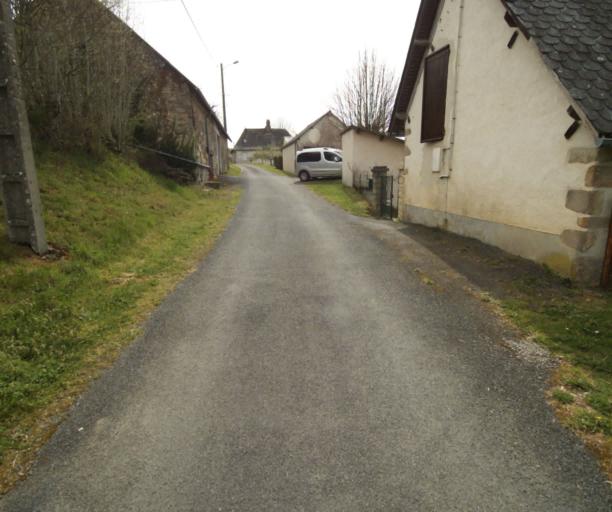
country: FR
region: Limousin
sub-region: Departement de la Correze
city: Sainte-Fortunade
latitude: 45.2052
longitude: 1.8522
